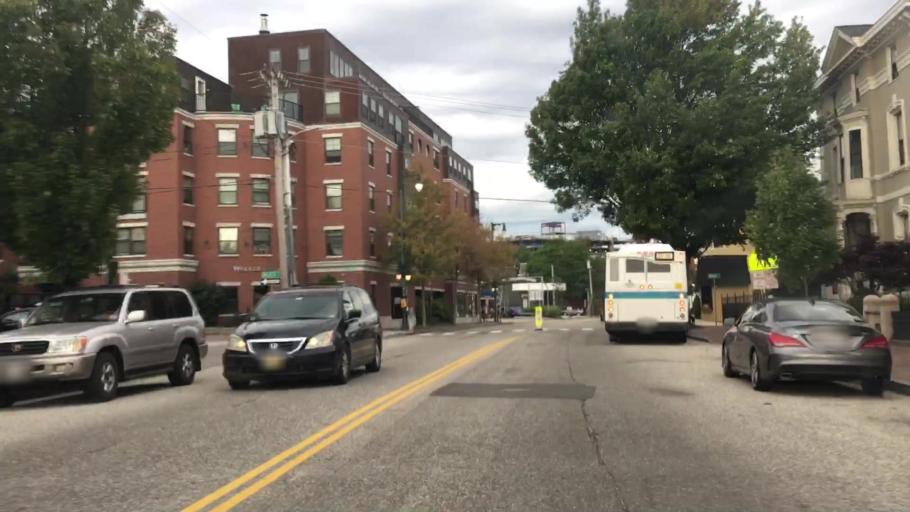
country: US
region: Maine
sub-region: Cumberland County
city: Portland
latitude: 43.6530
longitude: -70.2691
